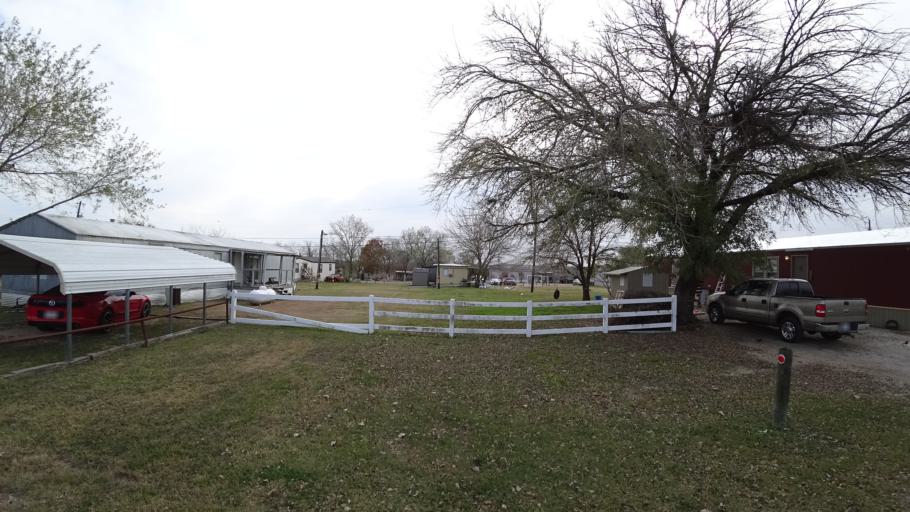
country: US
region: Texas
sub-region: Travis County
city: Garfield
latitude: 30.1488
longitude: -97.6671
